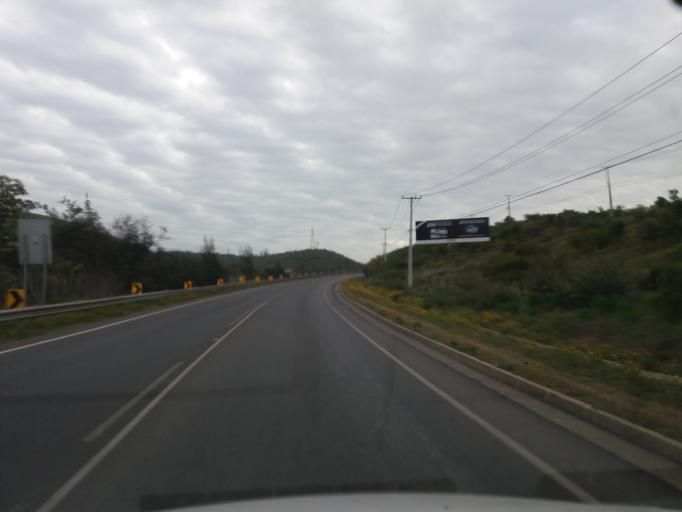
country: CL
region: Valparaiso
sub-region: Provincia de Marga Marga
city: Limache
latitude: -32.9506
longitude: -71.2845
